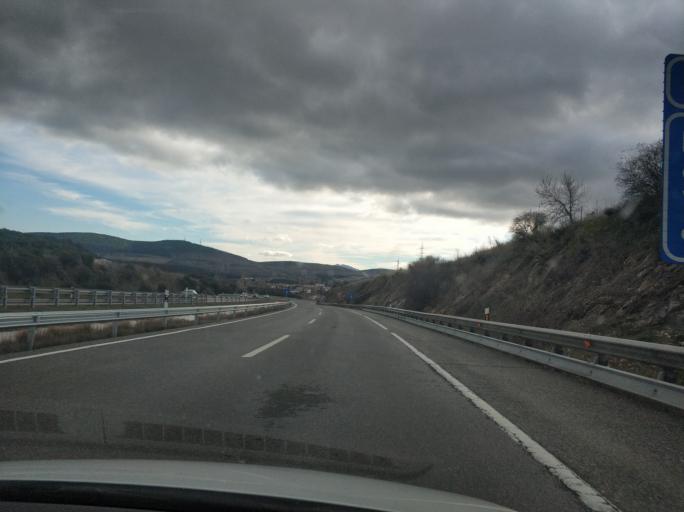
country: ES
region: Madrid
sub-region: Provincia de Madrid
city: Gascones
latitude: 41.0058
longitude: -3.6377
